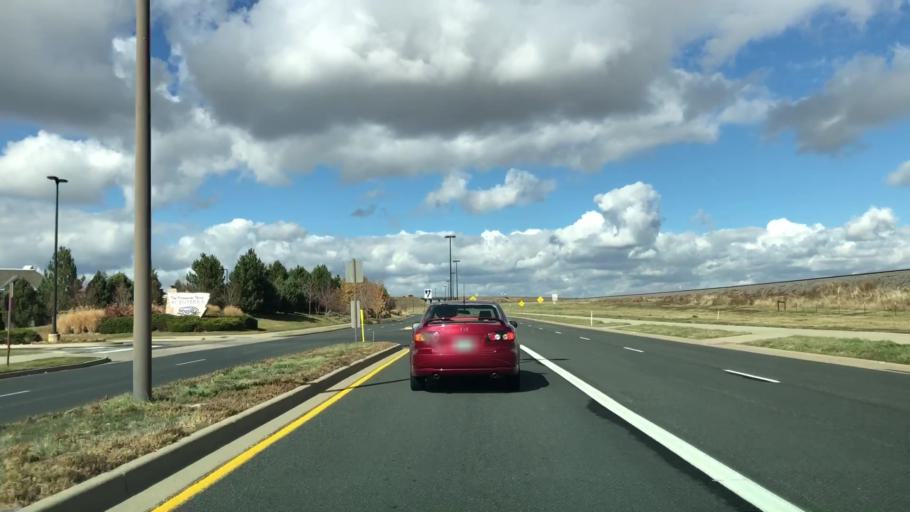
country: US
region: Colorado
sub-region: Larimer County
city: Loveland
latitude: 40.4181
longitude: -104.9870
